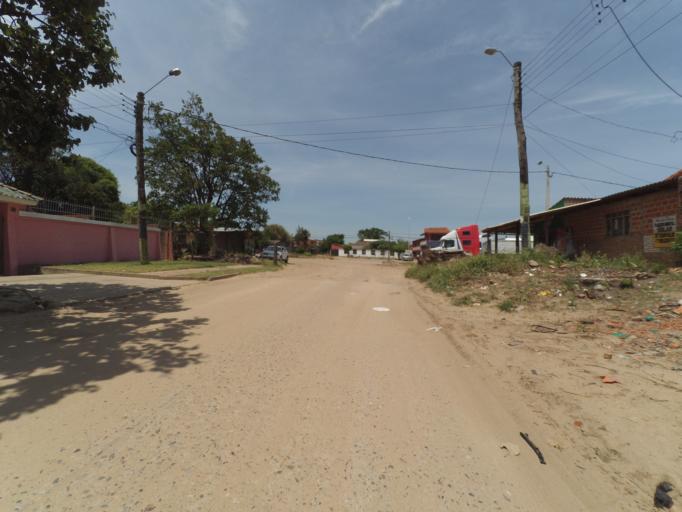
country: BO
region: Santa Cruz
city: Santa Cruz de la Sierra
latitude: -17.8282
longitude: -63.2317
